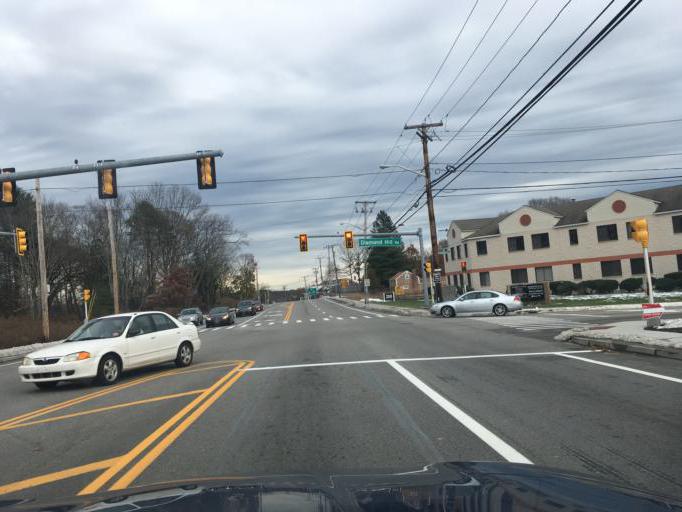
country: US
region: Rhode Island
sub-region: Kent County
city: East Greenwich
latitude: 41.6979
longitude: -71.4682
